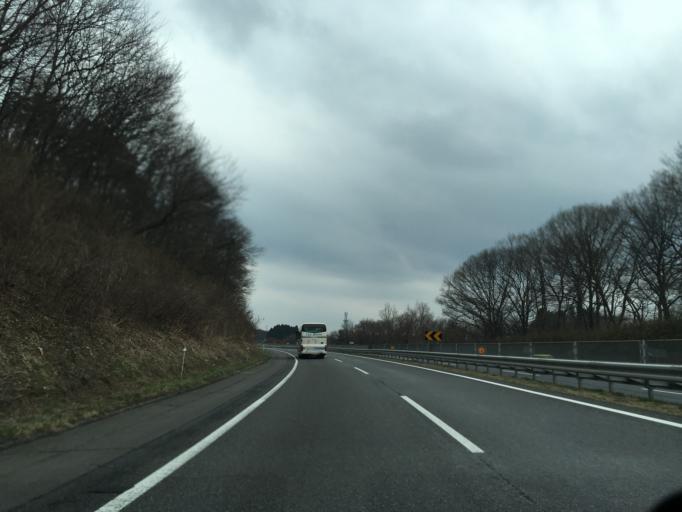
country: JP
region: Tochigi
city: Kuroiso
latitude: 37.0947
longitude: 140.1342
